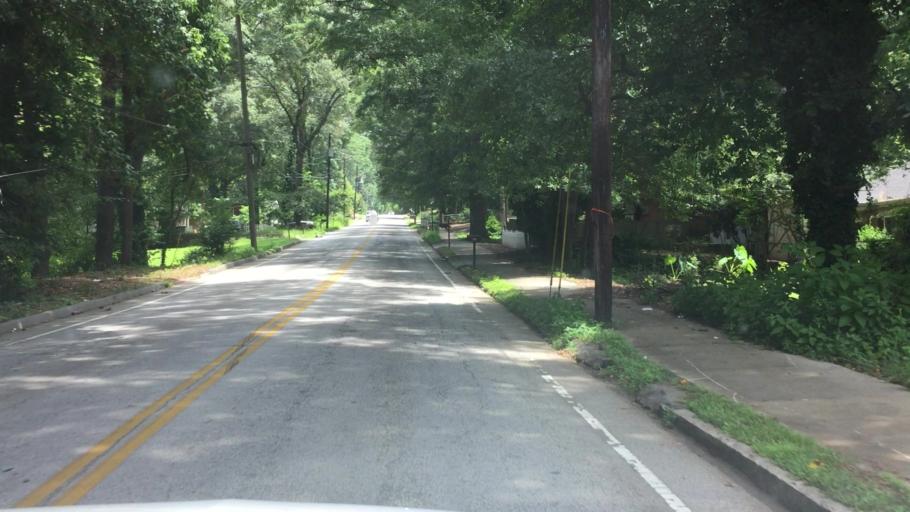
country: US
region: Georgia
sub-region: Fulton County
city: Atlanta
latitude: 33.7171
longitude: -84.3609
